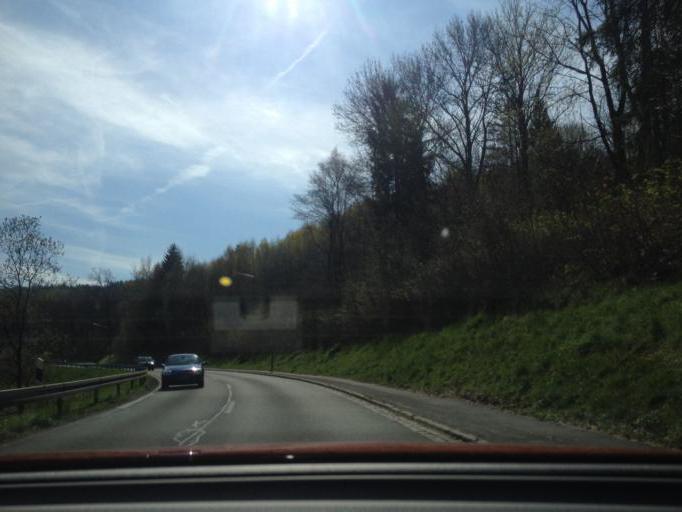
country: DE
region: Bavaria
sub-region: Upper Franconia
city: Gefrees
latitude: 50.0923
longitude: 11.7504
